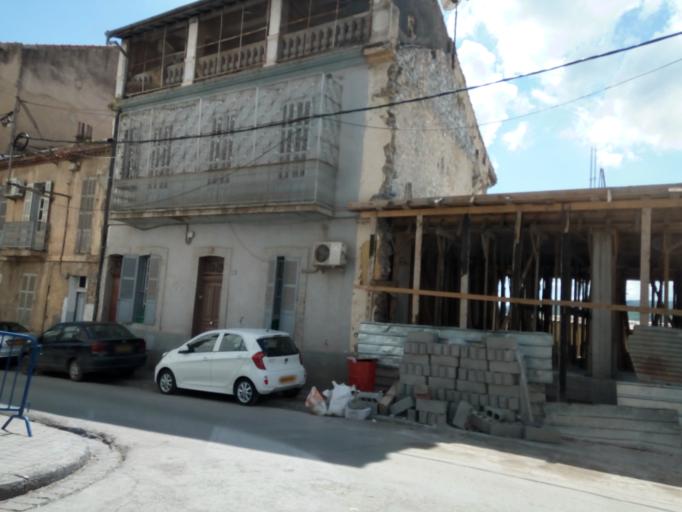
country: DZ
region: Constantine
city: Constantine
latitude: 36.3620
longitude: 6.6044
